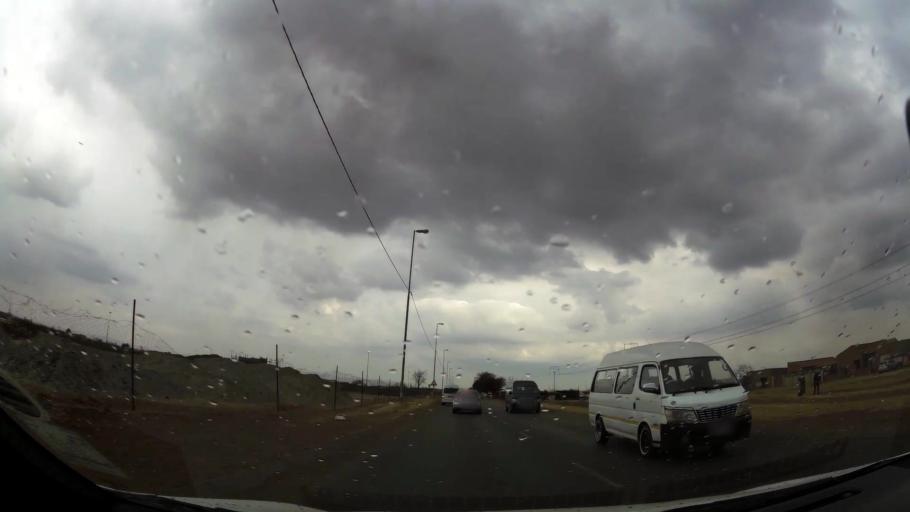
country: ZA
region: Gauteng
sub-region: Ekurhuleni Metropolitan Municipality
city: Germiston
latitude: -26.3532
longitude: 28.1441
